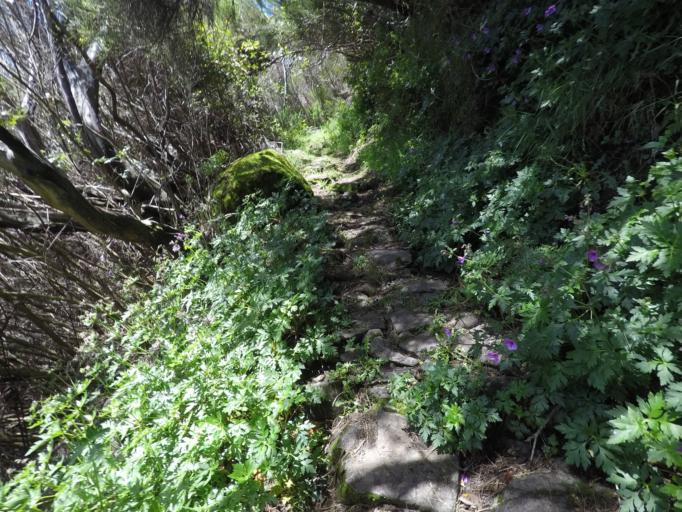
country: PT
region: Madeira
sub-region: Camara de Lobos
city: Curral das Freiras
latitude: 32.7546
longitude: -16.9741
